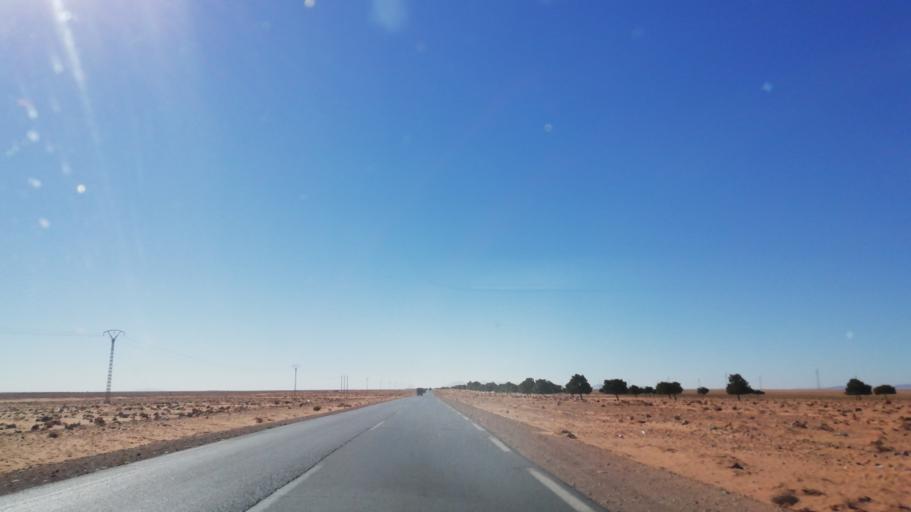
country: DZ
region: Wilaya de Naama
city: Naama
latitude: 33.9769
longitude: 0.0254
